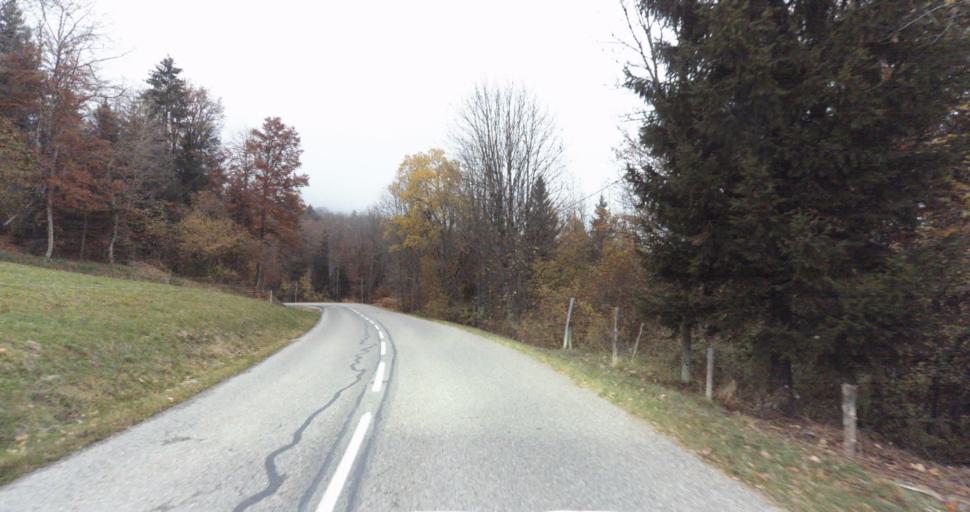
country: FR
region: Rhone-Alpes
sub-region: Departement de la Haute-Savoie
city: Saint-Jorioz
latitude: 45.7790
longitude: 6.1324
